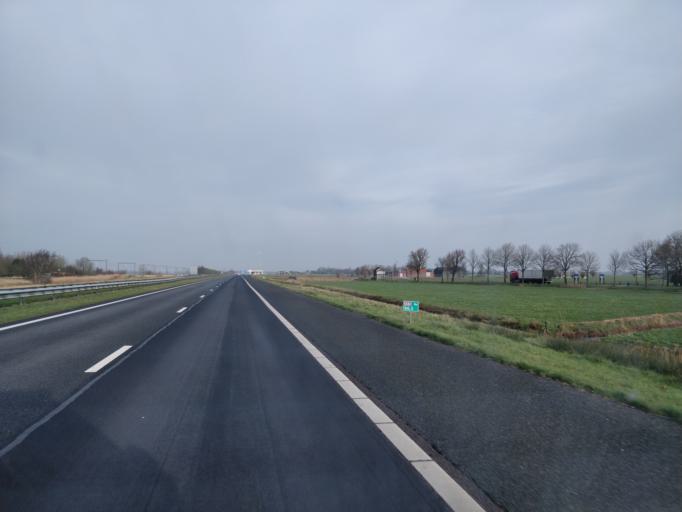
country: NL
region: Friesland
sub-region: Gemeente Boarnsterhim
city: Reduzum
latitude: 53.1212
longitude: 5.8083
